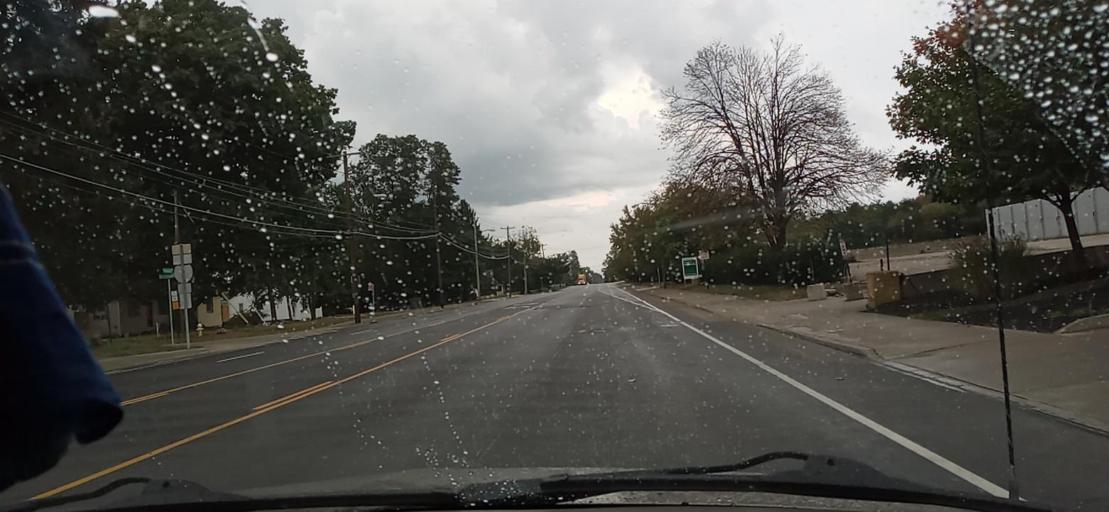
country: US
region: Ohio
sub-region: Summit County
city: Akron
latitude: 41.0689
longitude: -81.5696
